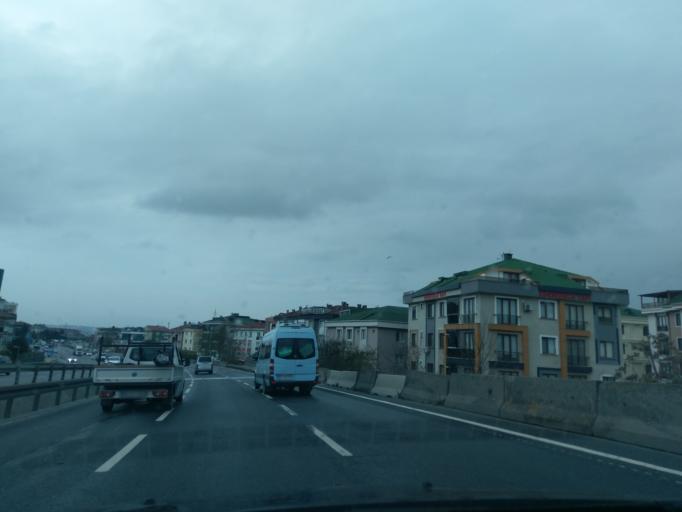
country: TR
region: Istanbul
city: Bueyuekcekmece
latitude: 41.0243
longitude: 28.5872
